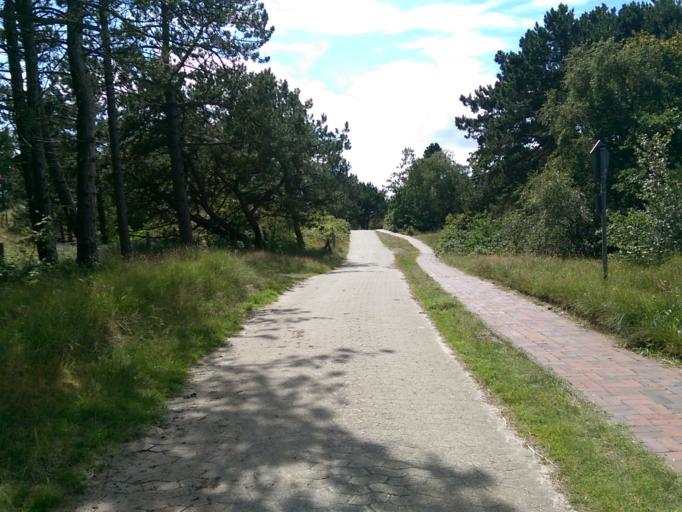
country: DE
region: Lower Saxony
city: Spiekeroog
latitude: 53.7730
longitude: 7.7039
